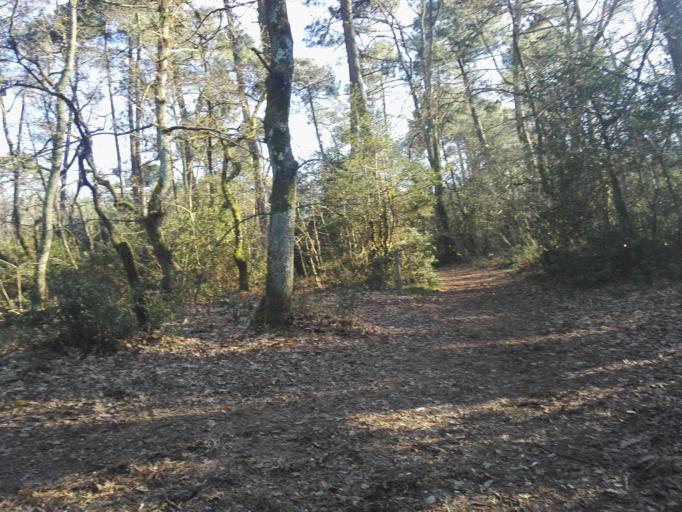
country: FR
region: Aquitaine
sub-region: Departement de la Gironde
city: Pessac
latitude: 44.8201
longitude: -0.6443
